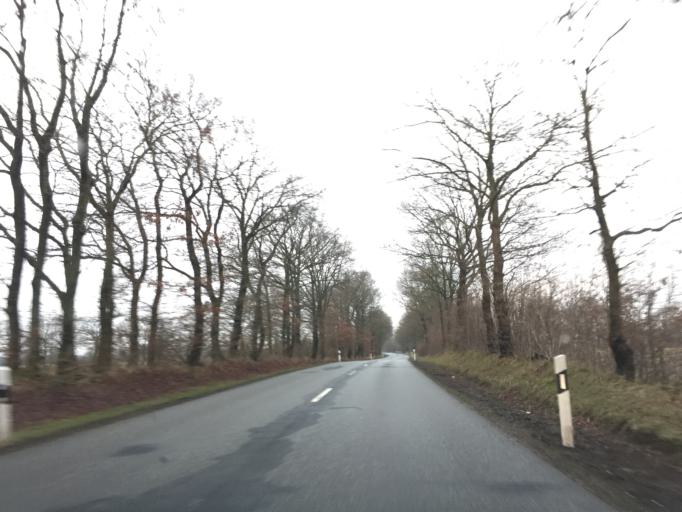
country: DE
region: Schleswig-Holstein
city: Wahlstedt
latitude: 53.9637
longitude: 10.1924
